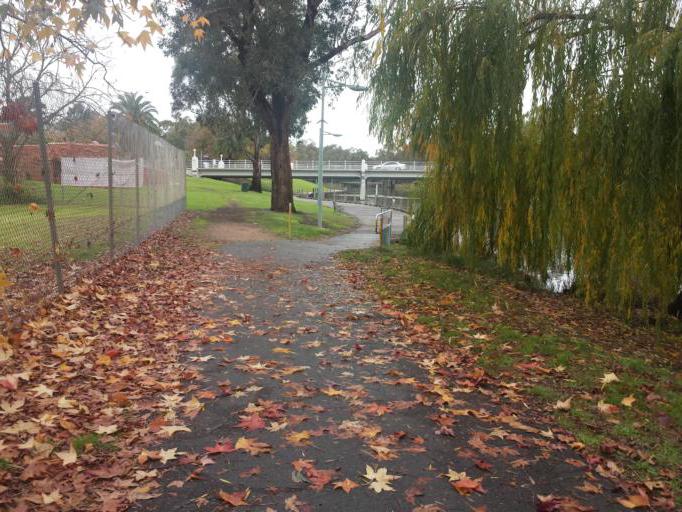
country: AU
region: Victoria
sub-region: Benalla
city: Benalla
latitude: -36.5516
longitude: 145.9808
